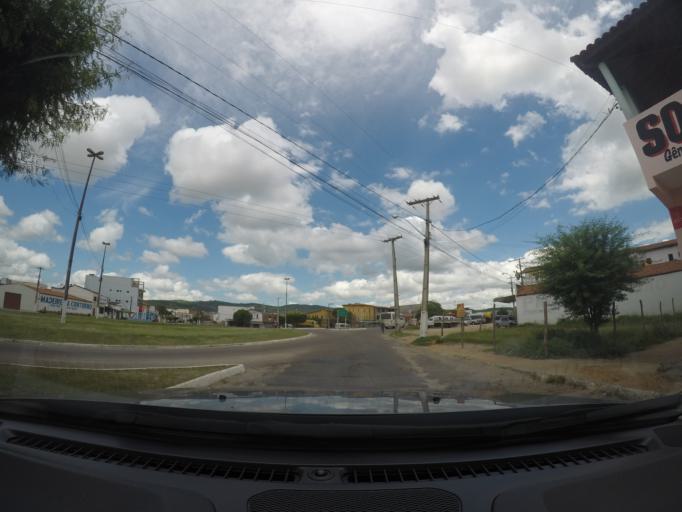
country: BR
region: Bahia
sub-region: Ipira
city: Ipira
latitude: -12.1620
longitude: -39.7453
